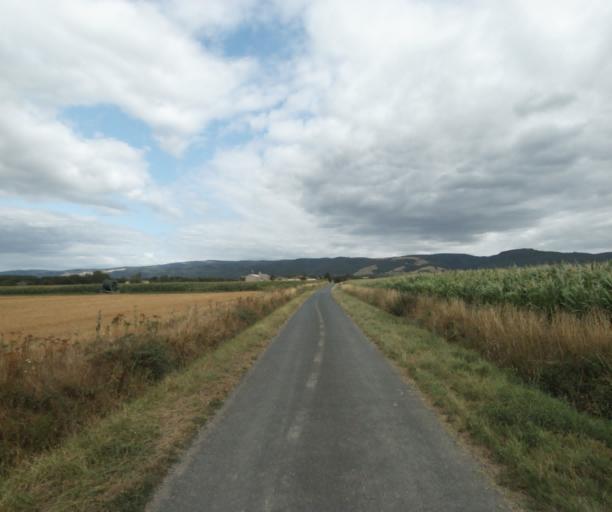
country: FR
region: Midi-Pyrenees
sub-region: Departement du Tarn
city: Soreze
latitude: 43.4731
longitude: 2.0529
